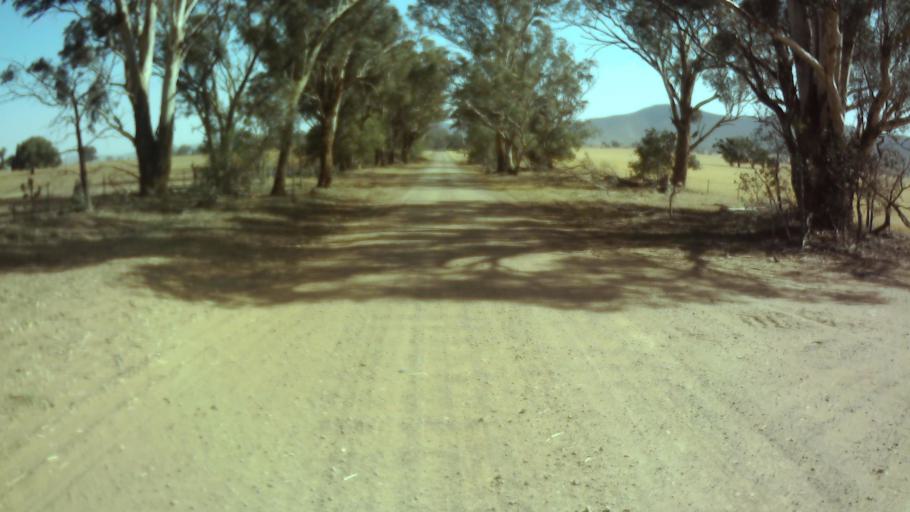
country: AU
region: New South Wales
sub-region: Weddin
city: Grenfell
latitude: -33.8495
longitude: 148.0167
